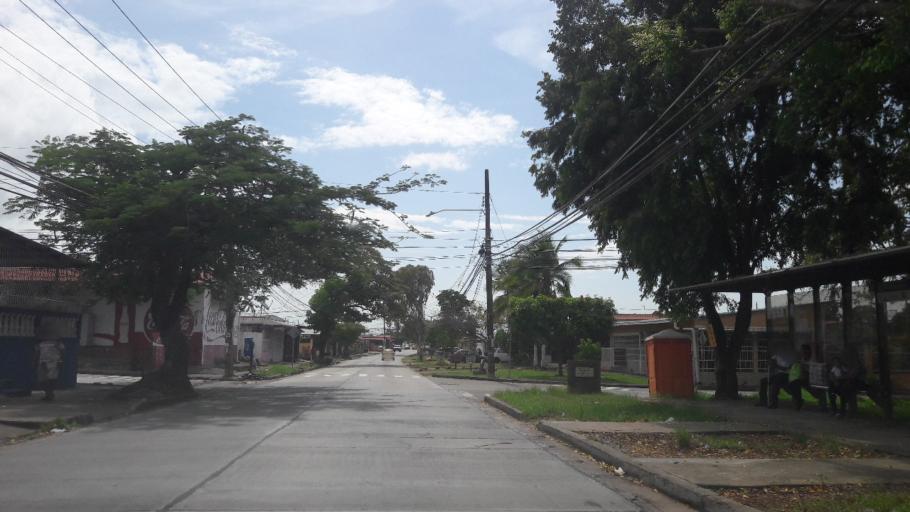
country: PA
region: Panama
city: Tocumen
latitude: 9.0593
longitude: -79.4196
